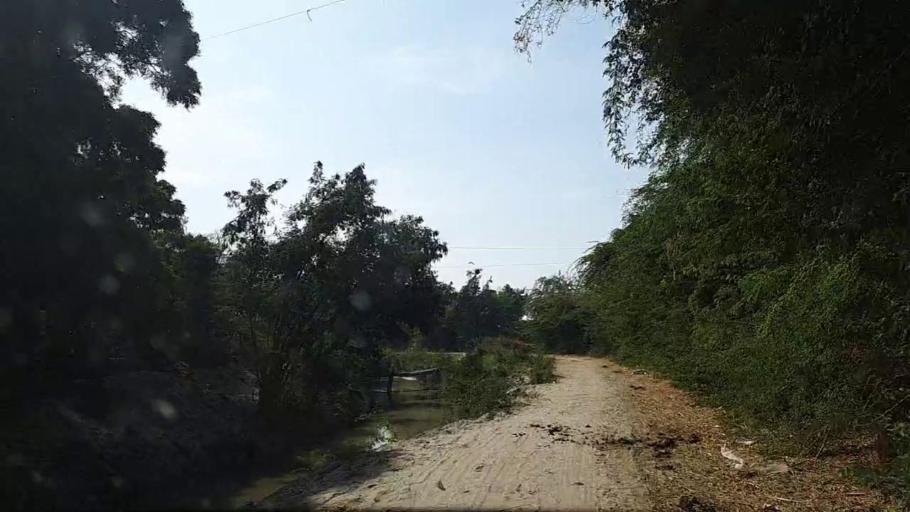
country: PK
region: Sindh
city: Daro Mehar
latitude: 24.7072
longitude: 68.1595
